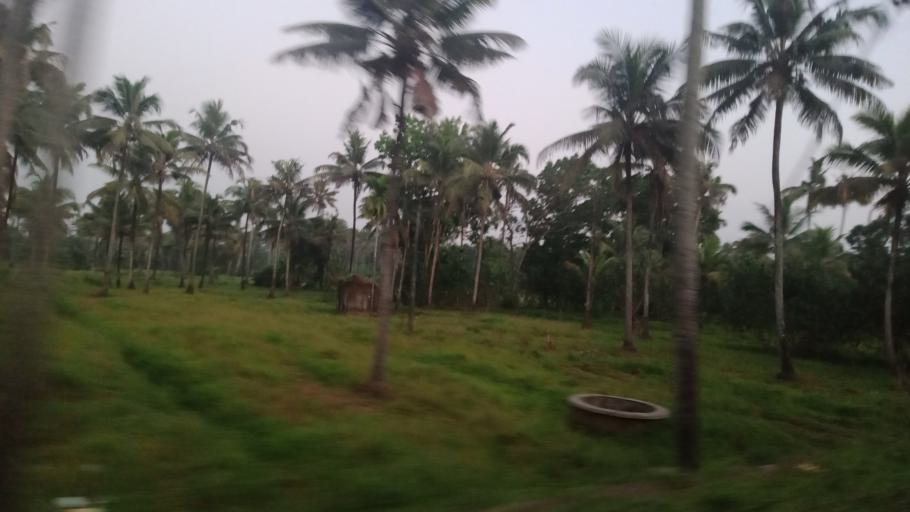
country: IN
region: Kerala
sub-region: Ernakulam
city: Angamali
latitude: 10.1949
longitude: 76.3090
